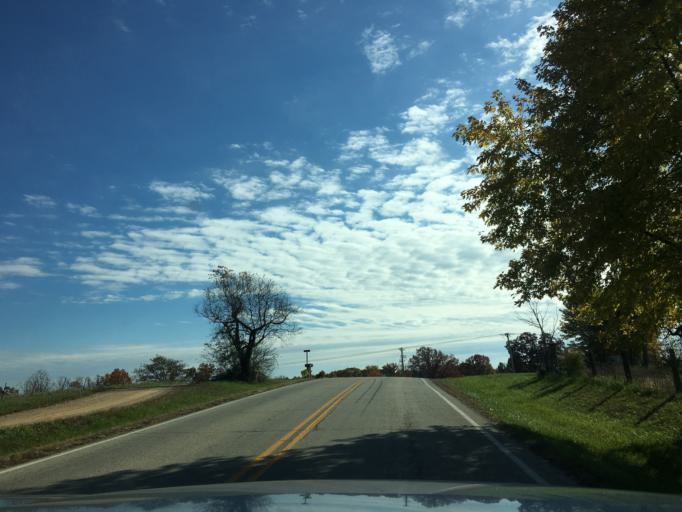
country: US
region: Missouri
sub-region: Osage County
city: Linn
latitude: 38.4263
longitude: -91.8252
